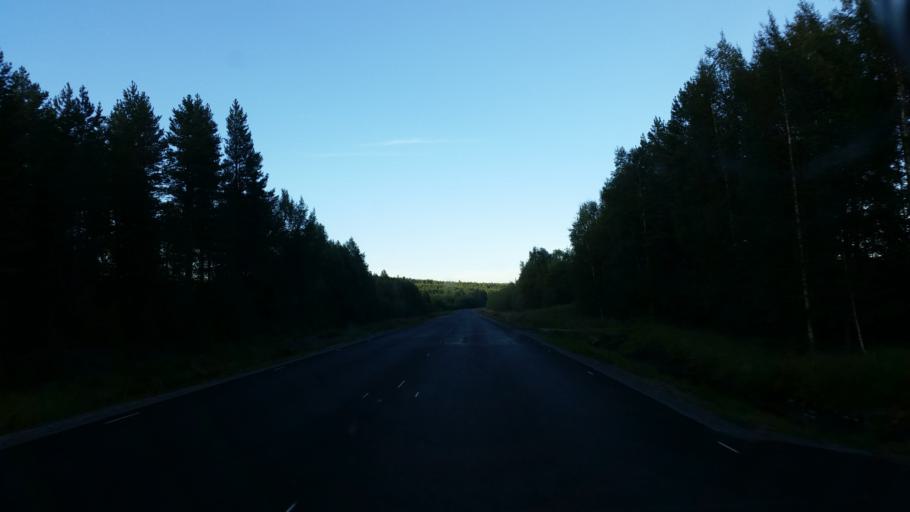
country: SE
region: Vaesterbotten
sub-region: Dorotea Kommun
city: Dorotea
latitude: 64.2961
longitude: 16.5453
